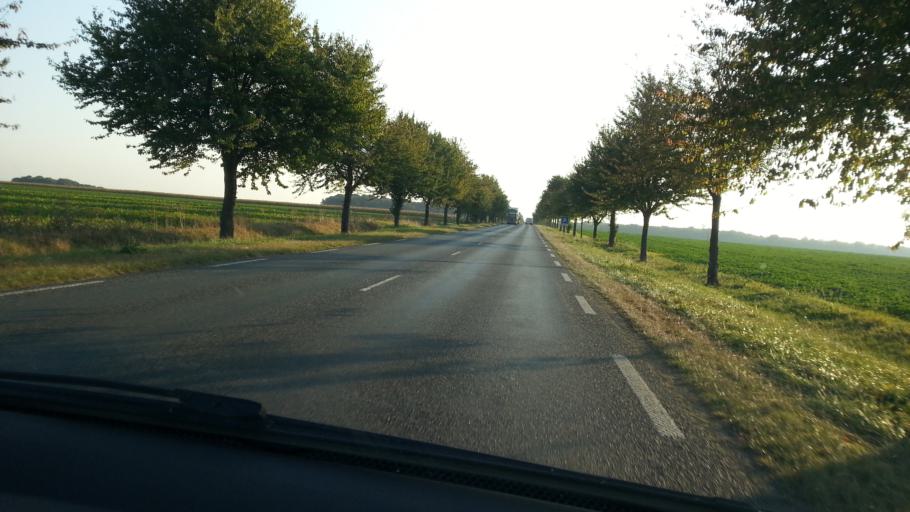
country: FR
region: Picardie
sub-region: Departement de l'Oise
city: Estrees-Saint-Denis
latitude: 49.4166
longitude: 2.6324
